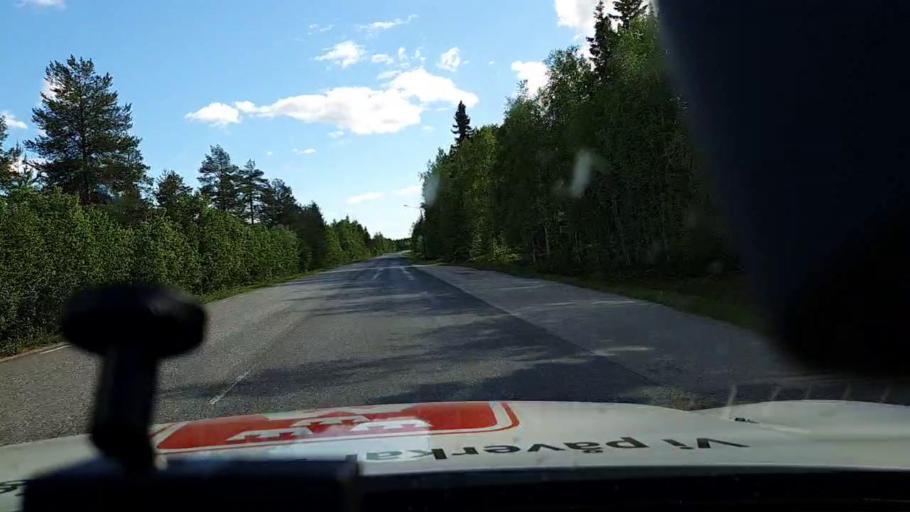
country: FI
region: Lapland
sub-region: Torniolaakso
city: Ylitornio
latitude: 66.3414
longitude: 23.6470
